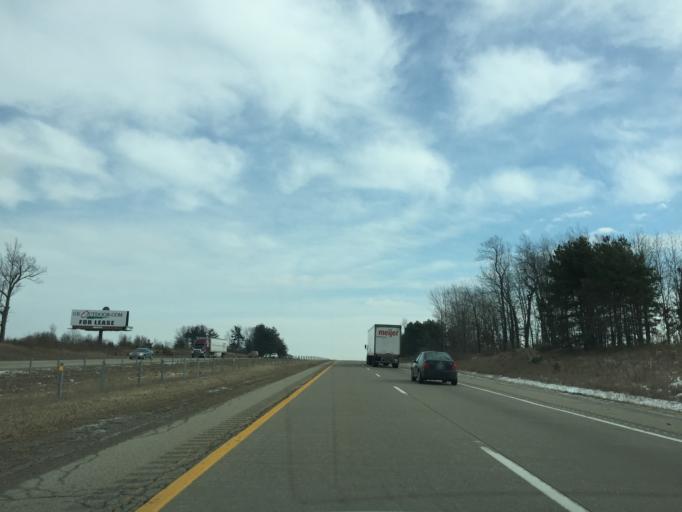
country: US
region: Michigan
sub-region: Ionia County
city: Saranac
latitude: 42.8793
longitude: -85.2557
